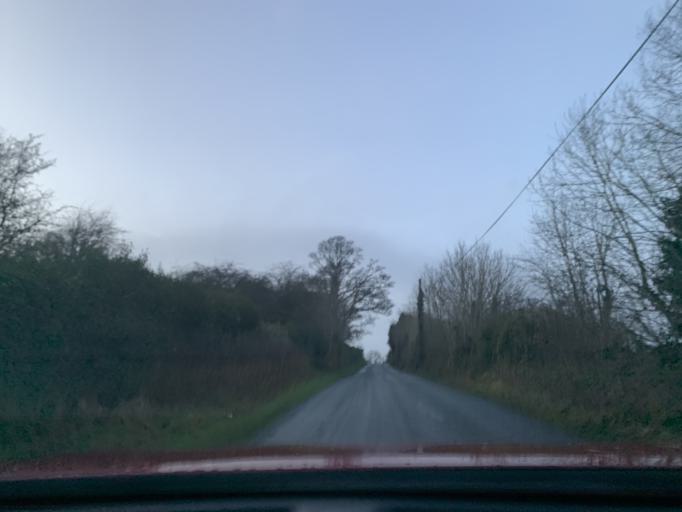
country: IE
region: Connaught
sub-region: Sligo
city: Ballymote
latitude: 54.1192
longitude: -8.5771
